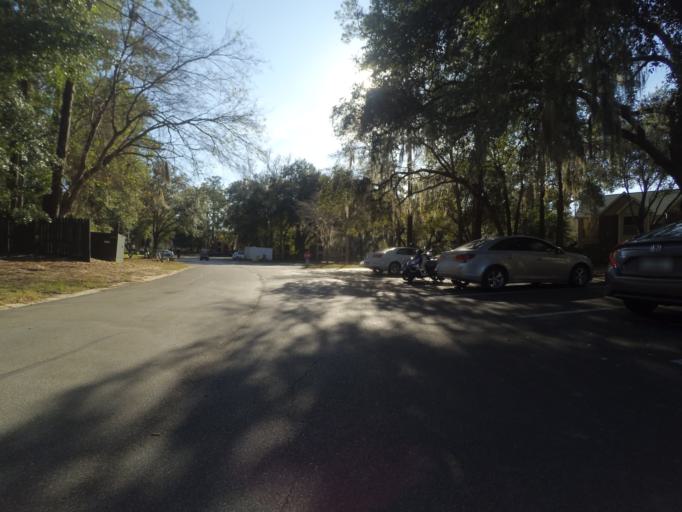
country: US
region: Florida
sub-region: Alachua County
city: Gainesville
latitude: 29.6170
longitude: -82.3576
